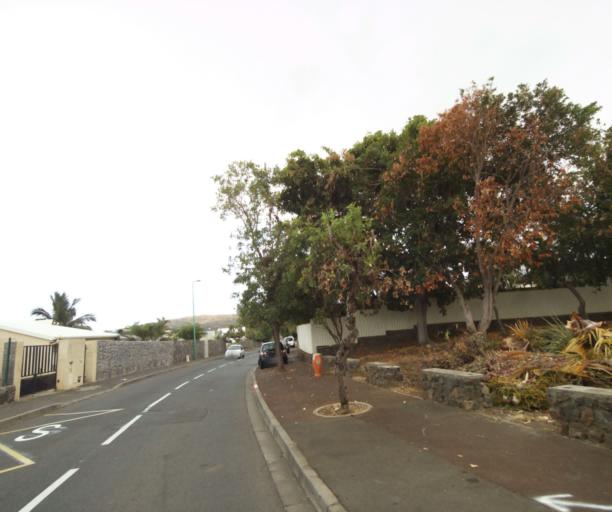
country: RE
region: Reunion
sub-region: Reunion
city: Saint-Paul
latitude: -21.0584
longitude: 55.2272
